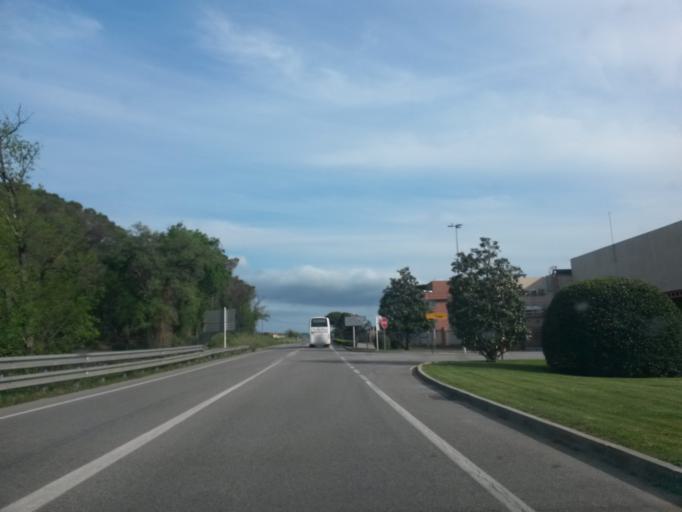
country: ES
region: Catalonia
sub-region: Provincia de Girona
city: Vidreres
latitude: 41.8016
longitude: 2.7714
